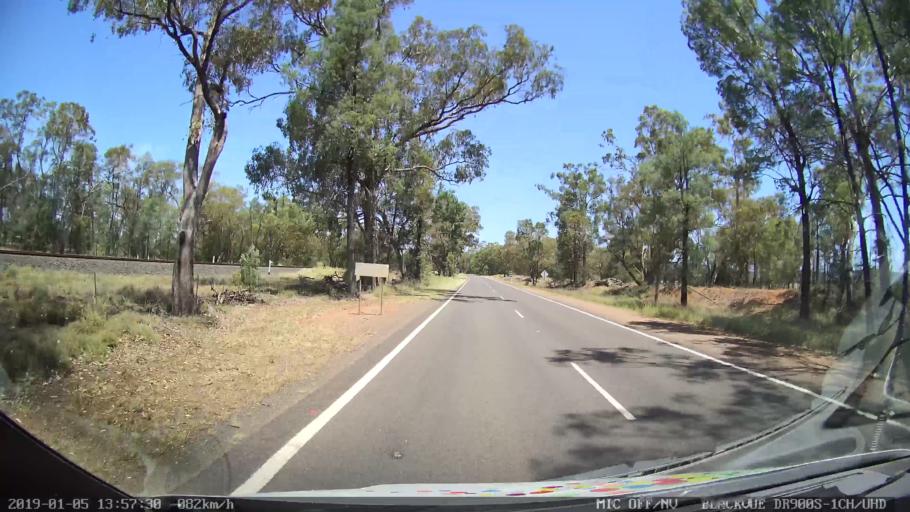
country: AU
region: New South Wales
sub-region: Gunnedah
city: Gunnedah
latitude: -31.1283
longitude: 150.2750
